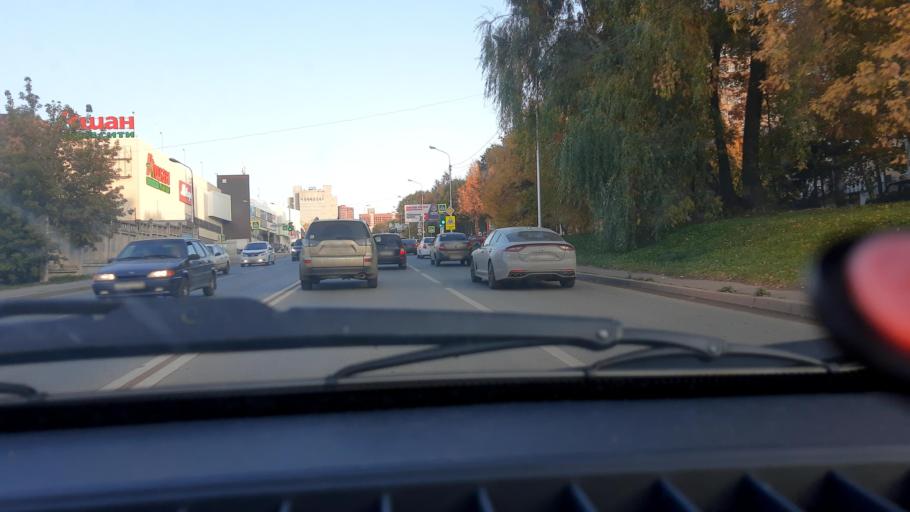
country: RU
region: Bashkortostan
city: Ufa
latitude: 54.7214
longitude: 55.9977
